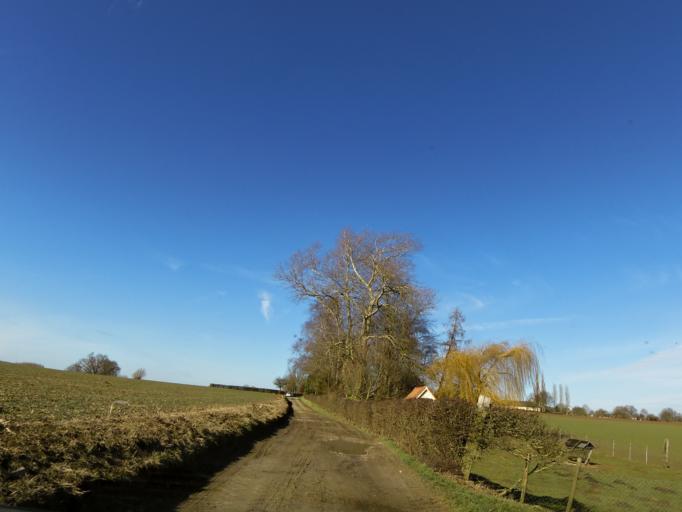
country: NL
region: Limburg
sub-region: Gemeente Voerendaal
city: Ubachsberg
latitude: 50.8367
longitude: 5.9463
